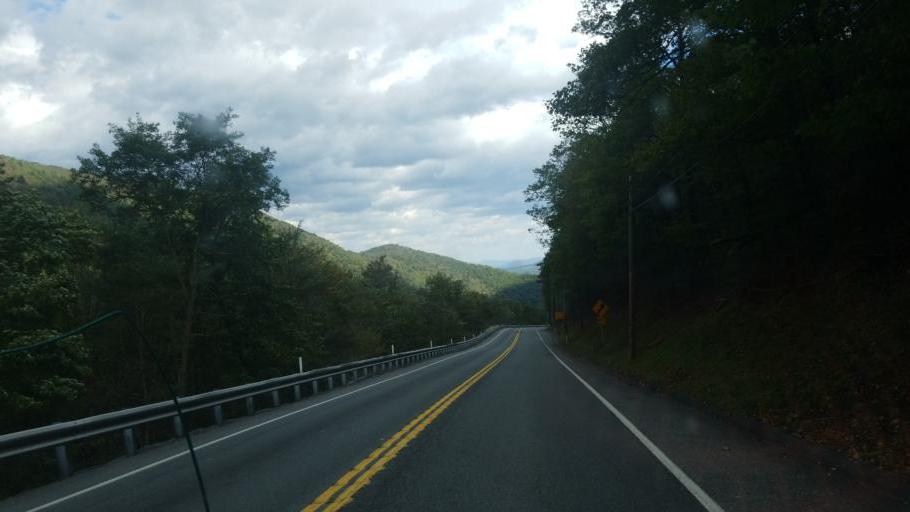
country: US
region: Pennsylvania
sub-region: Fulton County
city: McConnellsburg
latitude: 39.9276
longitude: -77.9360
